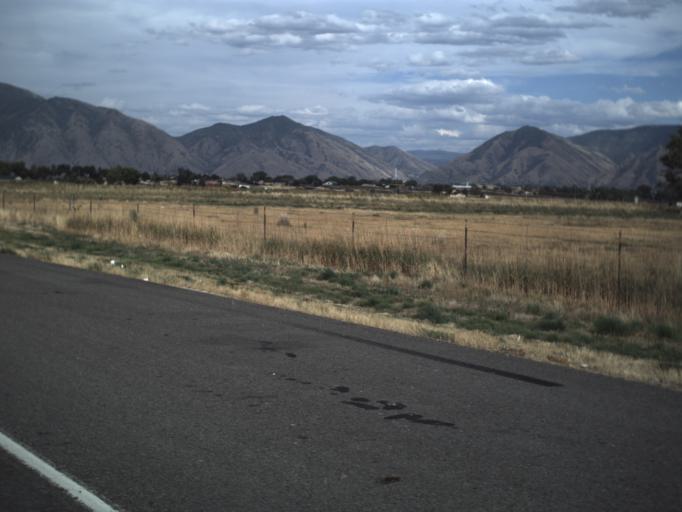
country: US
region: Utah
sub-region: Utah County
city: Benjamin
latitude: 40.0863
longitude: -111.7005
